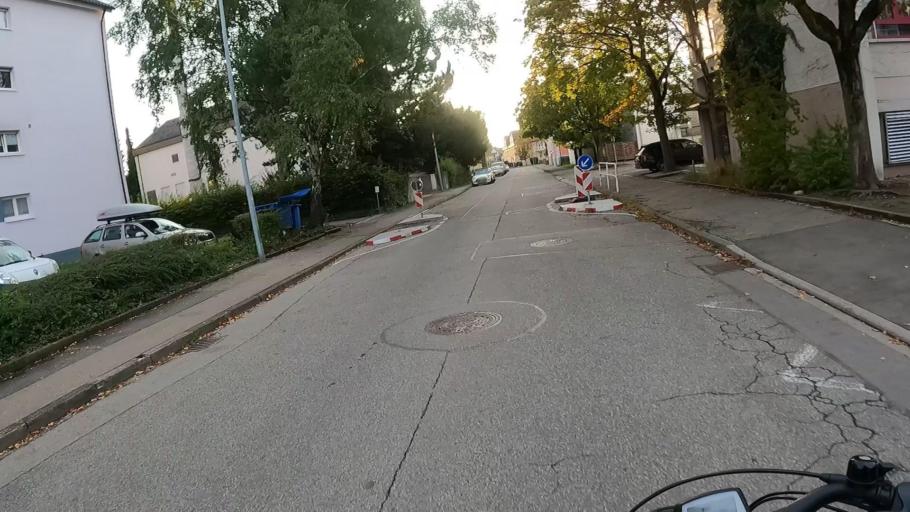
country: DE
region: Baden-Wuerttemberg
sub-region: Freiburg Region
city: Radolfzell am Bodensee
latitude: 47.7422
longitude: 8.9653
